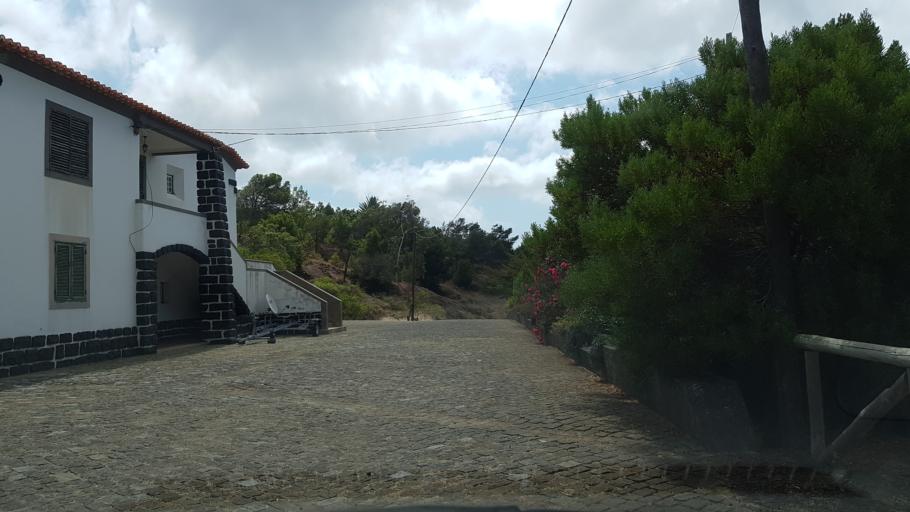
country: PT
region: Madeira
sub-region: Porto Santo
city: Vila de Porto Santo
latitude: 33.0667
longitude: -16.3352
